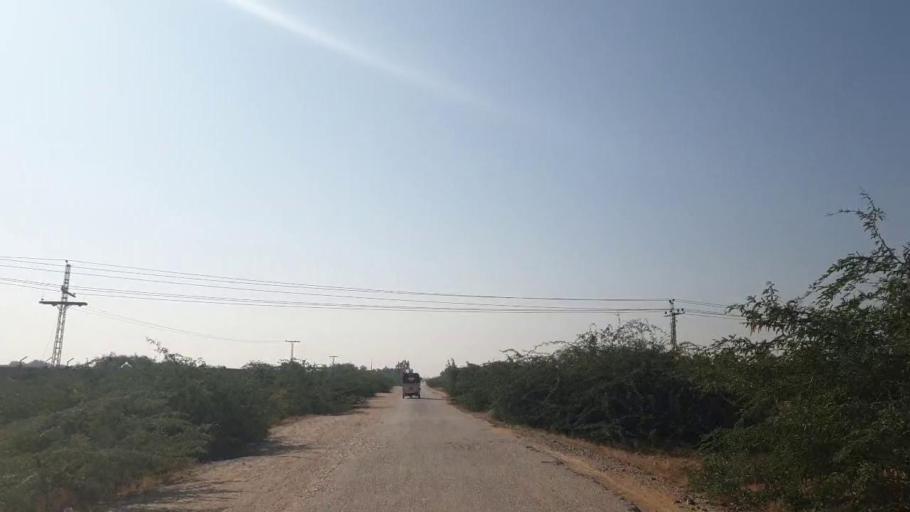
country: PK
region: Sindh
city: Thatta
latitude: 25.1484
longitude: 67.7735
